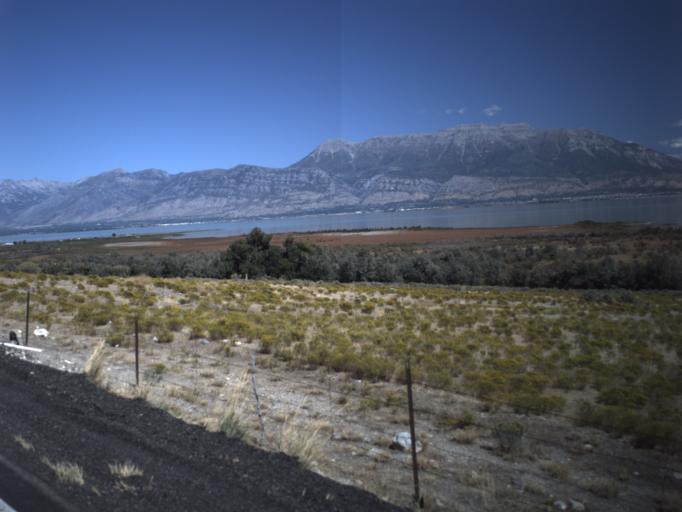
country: US
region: Utah
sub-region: Utah County
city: Saratoga Springs
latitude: 40.2469
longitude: -111.8661
